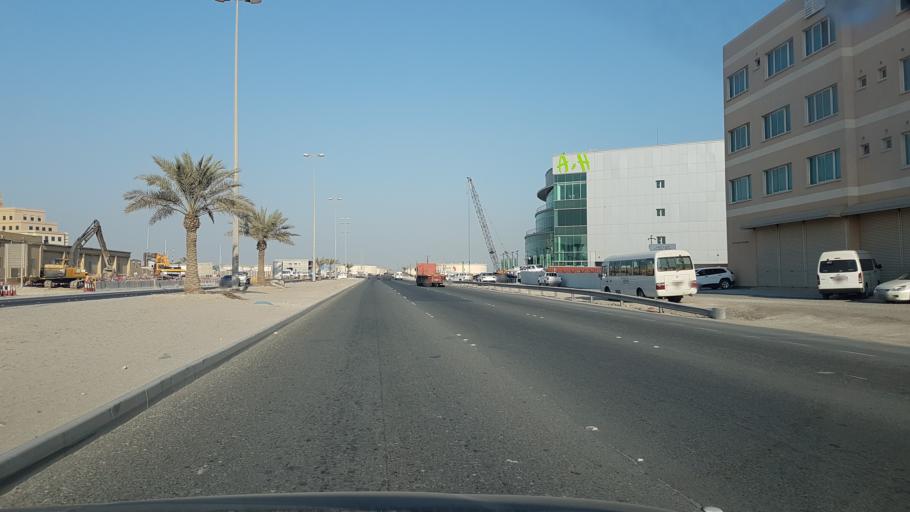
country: BH
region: Northern
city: Sitrah
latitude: 26.1399
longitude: 50.6129
